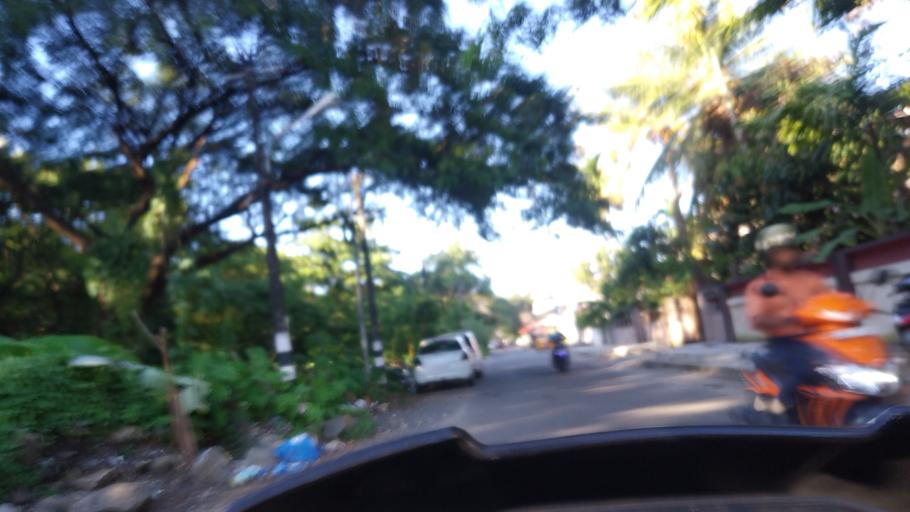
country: IN
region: Kerala
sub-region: Ernakulam
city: Cochin
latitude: 9.9953
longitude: 76.2776
